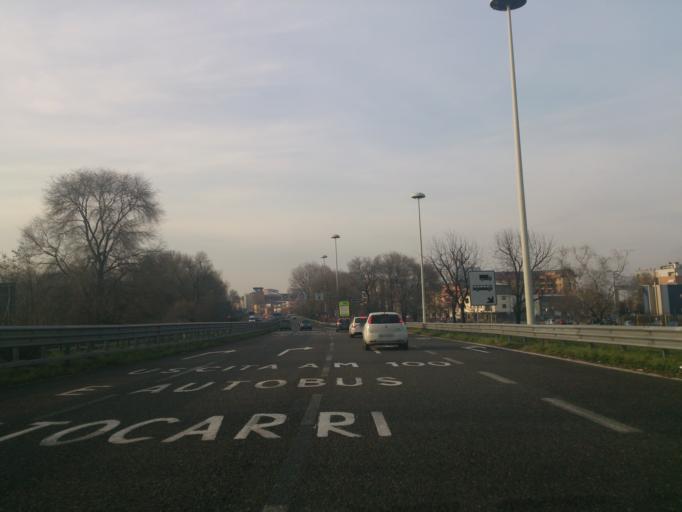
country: IT
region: Lombardy
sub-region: Citta metropolitana di Milano
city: Chiaravalle
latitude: 45.4331
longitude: 9.2367
